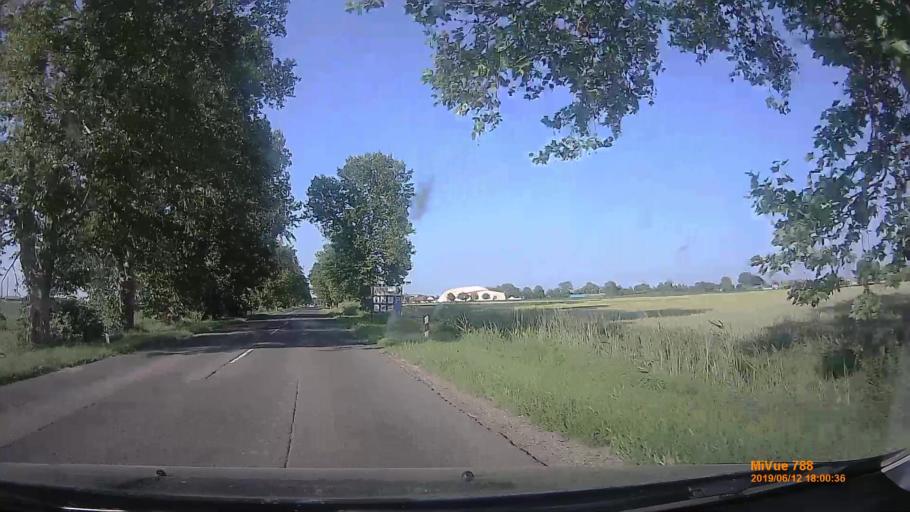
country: HU
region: Csongrad
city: Roszke
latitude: 46.2186
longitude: 20.0636
